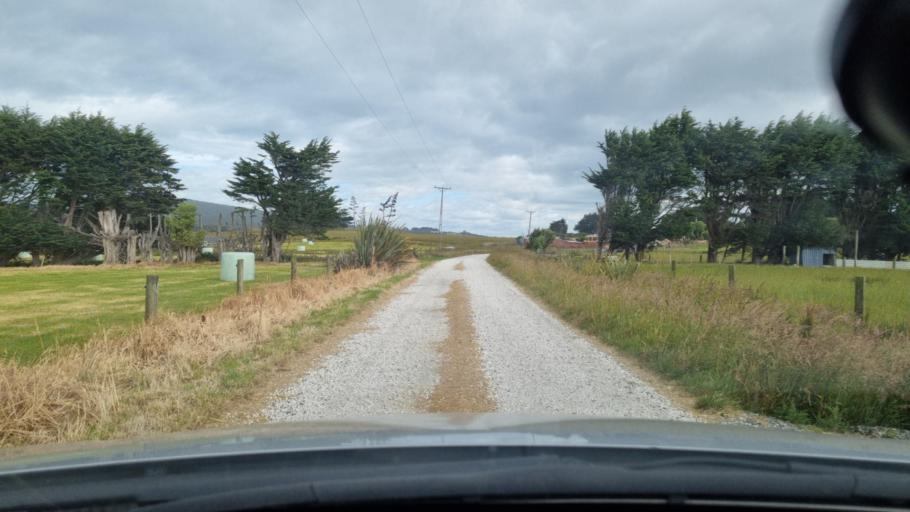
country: NZ
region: Southland
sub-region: Invercargill City
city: Bluff
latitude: -46.5409
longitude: 168.2915
